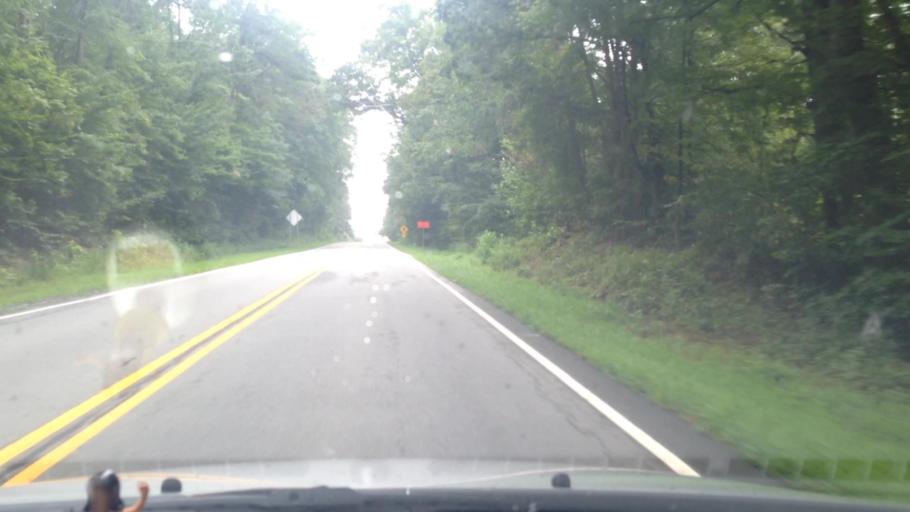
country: US
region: North Carolina
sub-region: Stokes County
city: Danbury
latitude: 36.3994
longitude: -80.1400
